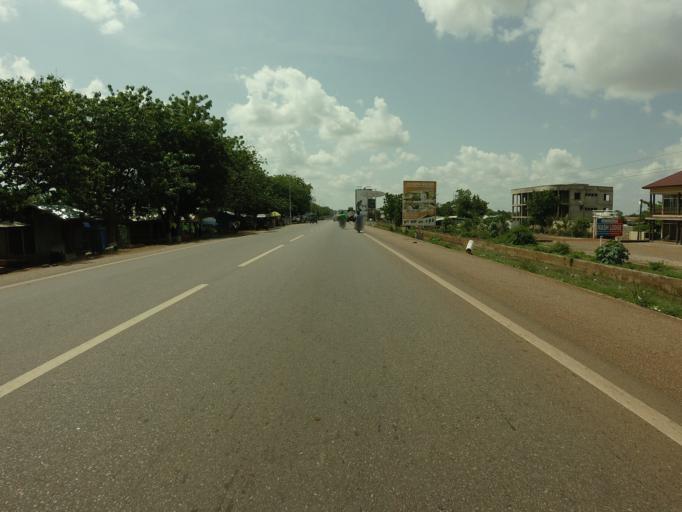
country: GH
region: Northern
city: Tamale
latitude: 9.4398
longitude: -0.8437
